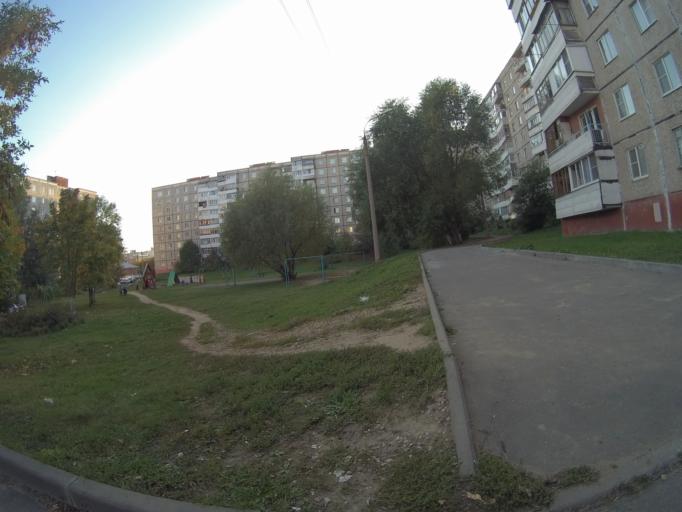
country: RU
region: Vladimir
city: Vladimir
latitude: 56.1095
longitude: 40.3529
